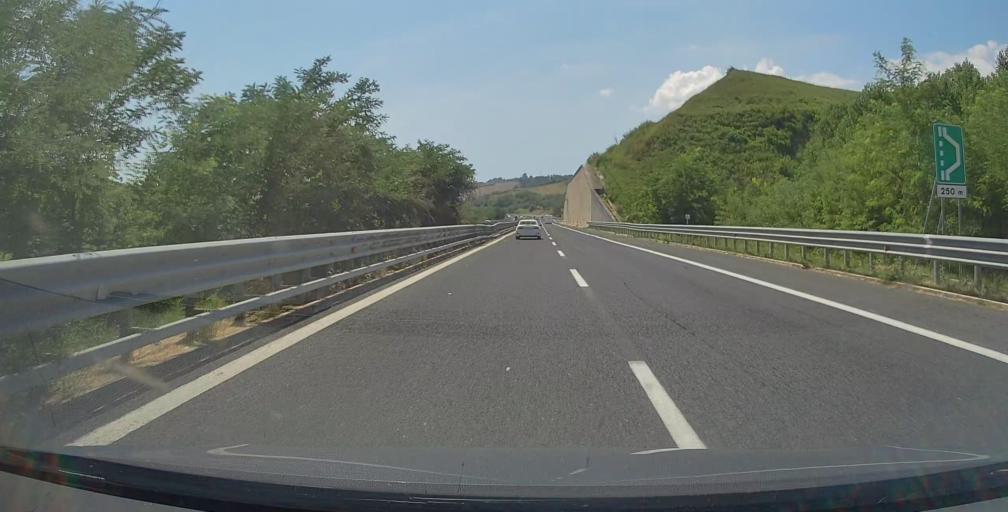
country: IT
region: Calabria
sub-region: Provincia di Vibo-Valentia
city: Francica
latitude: 38.5740
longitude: 16.1023
